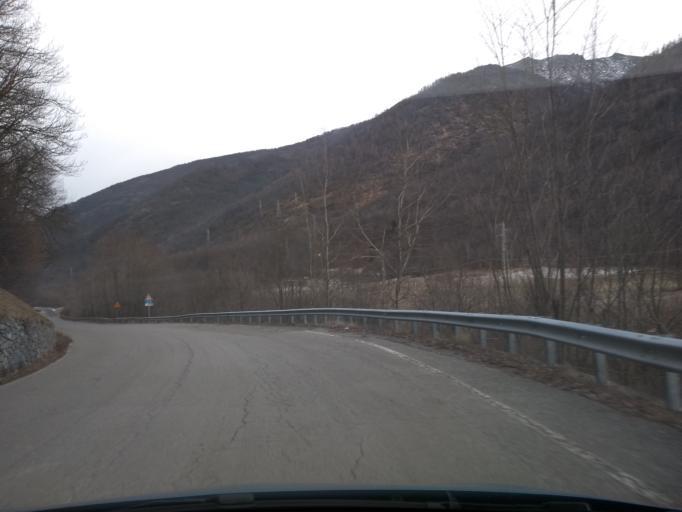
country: IT
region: Piedmont
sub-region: Provincia di Torino
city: Lemie
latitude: 45.2237
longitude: 7.3224
